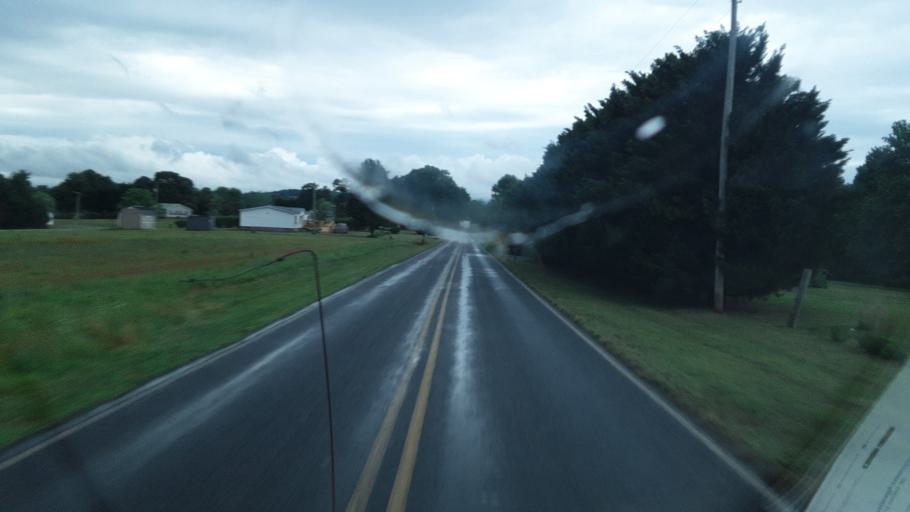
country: US
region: North Carolina
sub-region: Yadkin County
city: Jonesville
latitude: 36.0968
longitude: -80.8688
